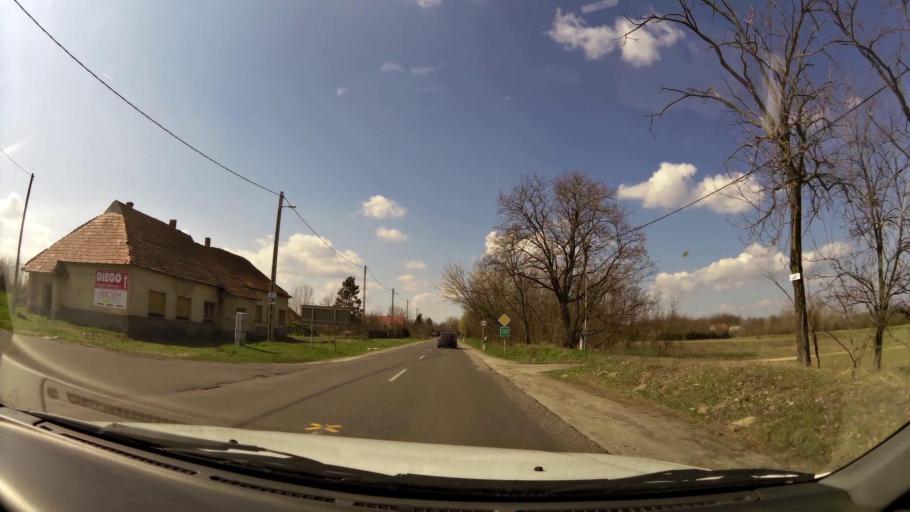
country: HU
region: Pest
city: Farmos
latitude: 47.3653
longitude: 19.8051
